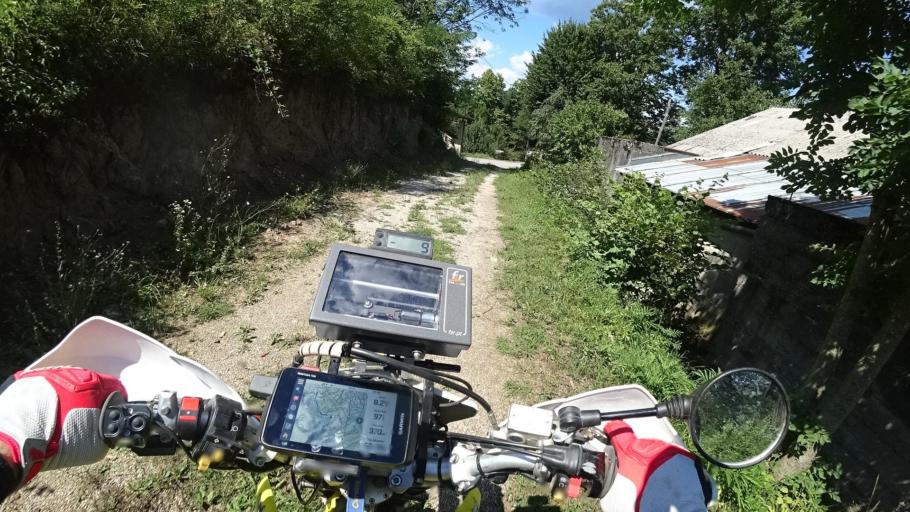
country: HR
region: Karlovacka
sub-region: Grad Ogulin
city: Ogulin
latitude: 45.2530
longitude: 15.2170
